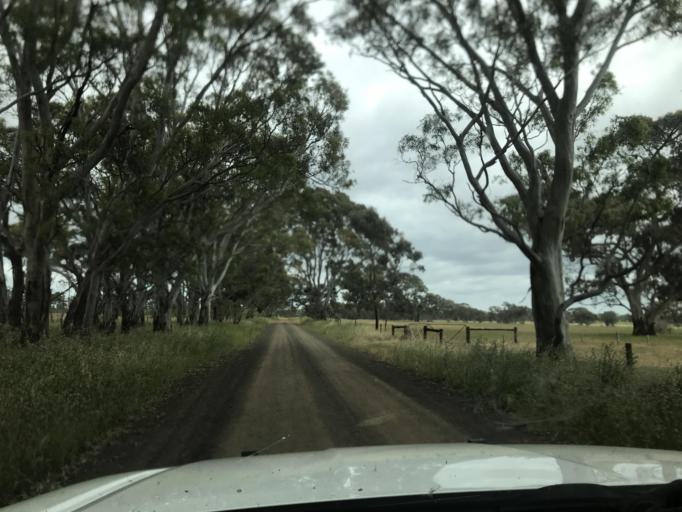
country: AU
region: South Australia
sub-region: Wattle Range
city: Penola
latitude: -37.1025
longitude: 141.2373
